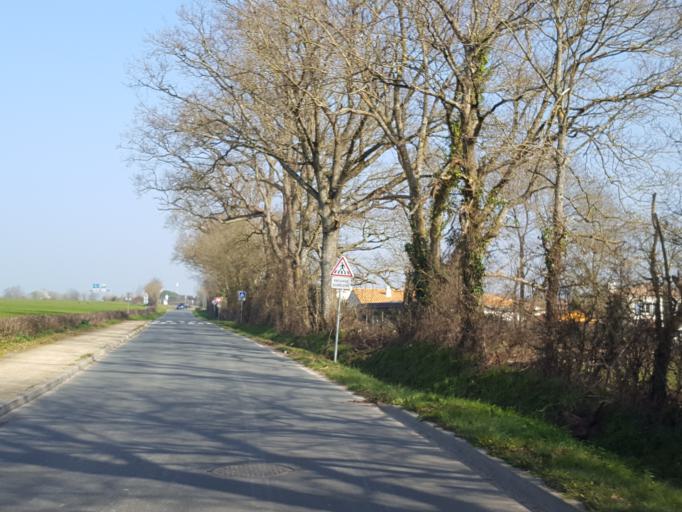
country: FR
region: Pays de la Loire
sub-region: Departement de la Vendee
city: La Roche-sur-Yon
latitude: 46.6747
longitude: -1.4503
